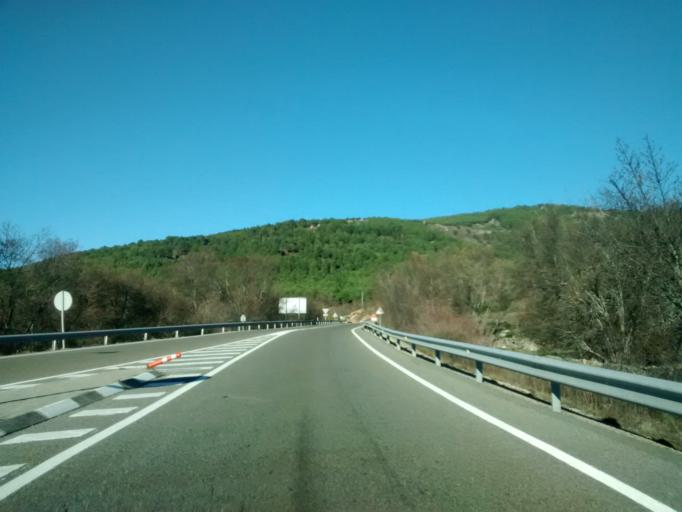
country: ES
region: Madrid
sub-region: Provincia de Madrid
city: Navacerrada
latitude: 40.7340
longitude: -4.0071
